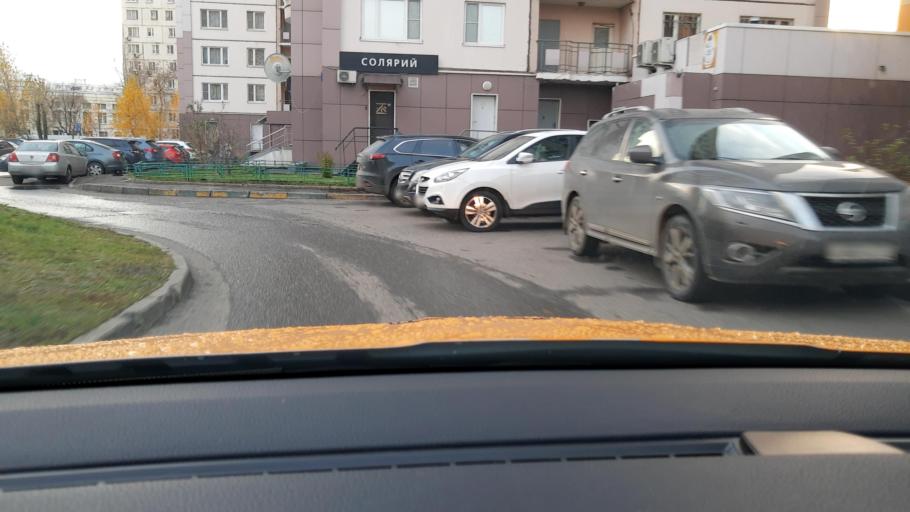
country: RU
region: Moscow
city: Altuf'yevskiy
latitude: 55.8750
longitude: 37.5896
